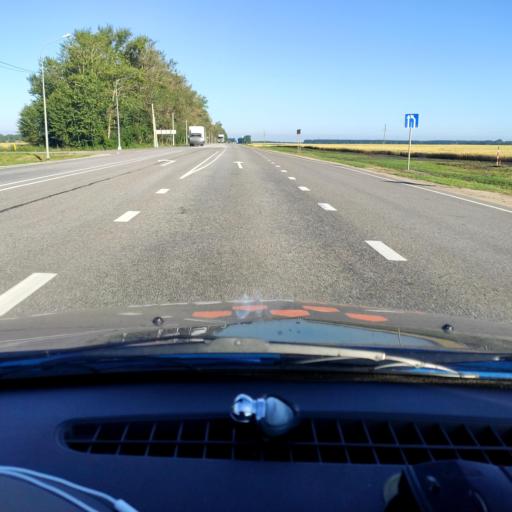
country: RU
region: Orjol
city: Pokrovskoye
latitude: 52.6286
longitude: 36.7083
